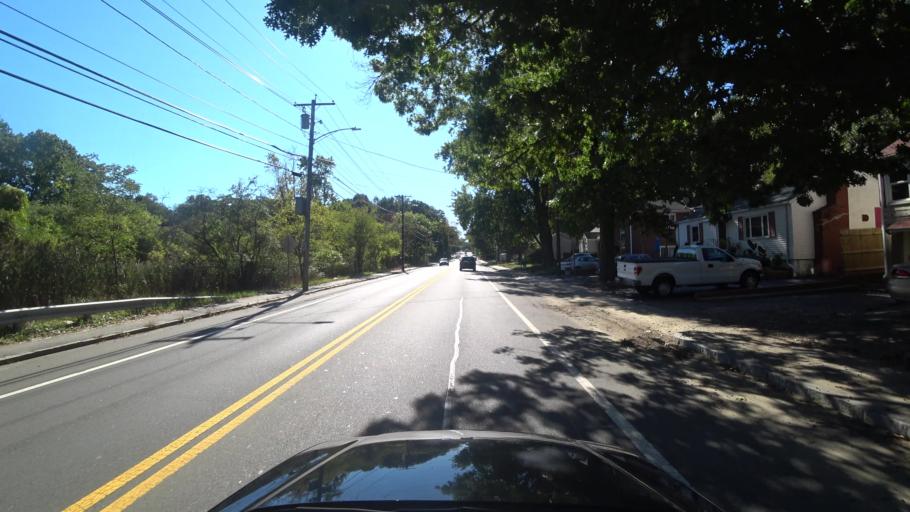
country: US
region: Massachusetts
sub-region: Essex County
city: Salem
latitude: 42.4909
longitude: -70.8955
